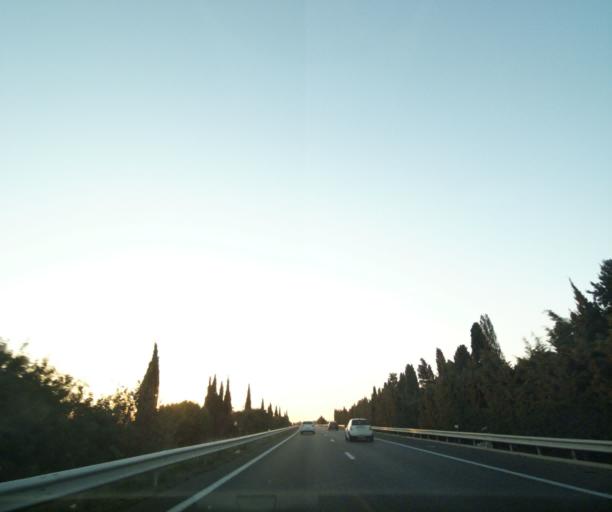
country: FR
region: Provence-Alpes-Cote d'Azur
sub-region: Departement des Bouches-du-Rhone
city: Mouries
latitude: 43.6393
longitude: 4.8729
